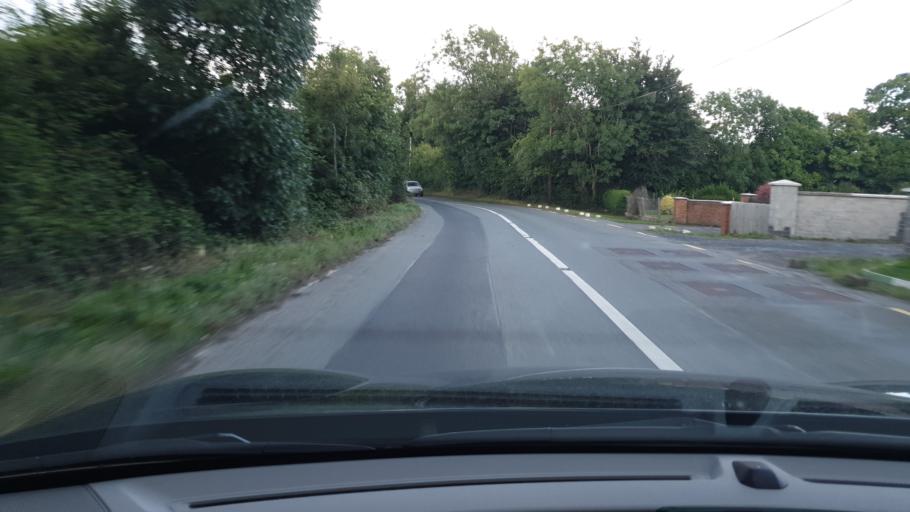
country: IE
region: Leinster
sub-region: South Dublin
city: Saggart
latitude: 53.3115
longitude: -6.4505
